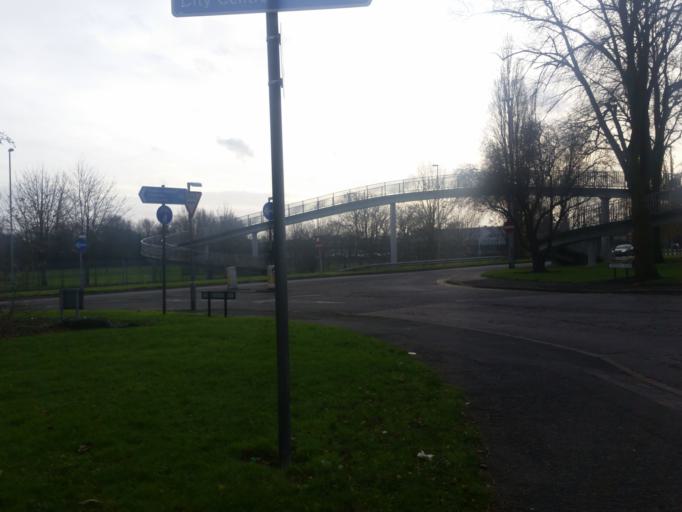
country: GB
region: England
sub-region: Derbyshire
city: Long Eaton
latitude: 52.9155
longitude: -1.2314
